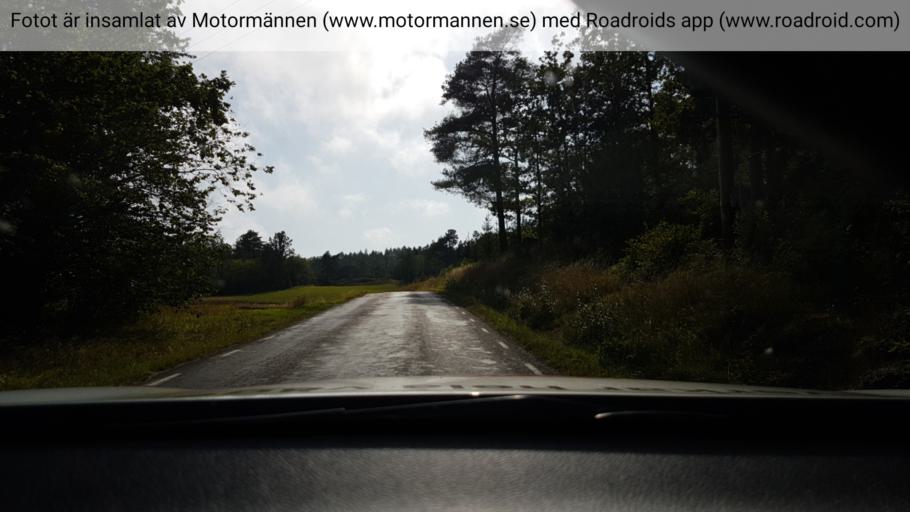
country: SE
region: Stockholm
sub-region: Nynashamns Kommun
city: Osmo
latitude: 58.8954
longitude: 17.7948
